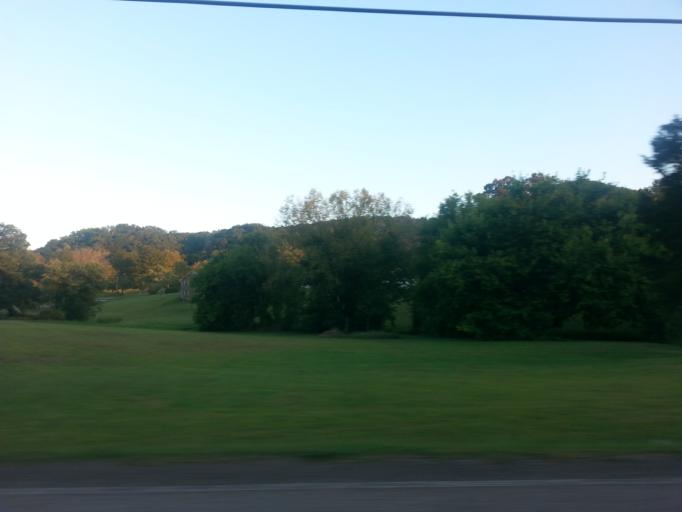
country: US
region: Tennessee
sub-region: Sevier County
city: Seymour
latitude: 35.9219
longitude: -83.7733
